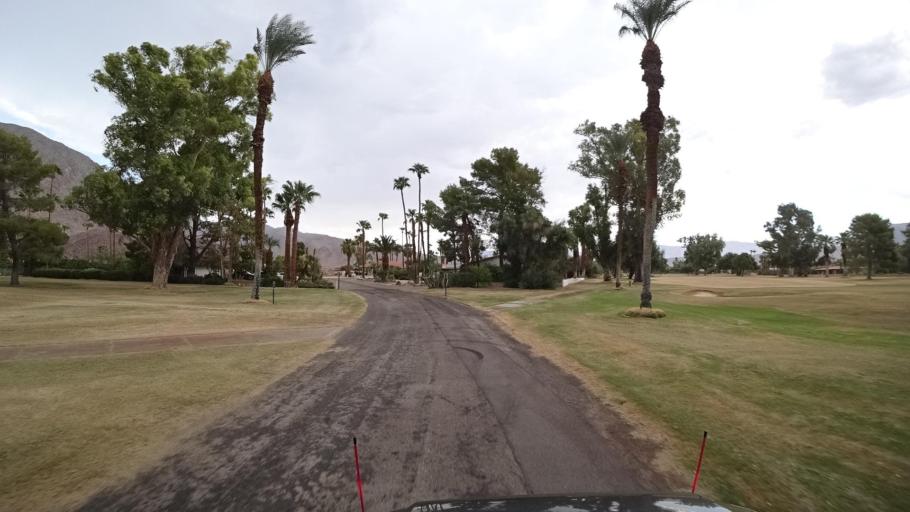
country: US
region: California
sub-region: San Diego County
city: Borrego Springs
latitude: 33.2882
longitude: -116.3901
